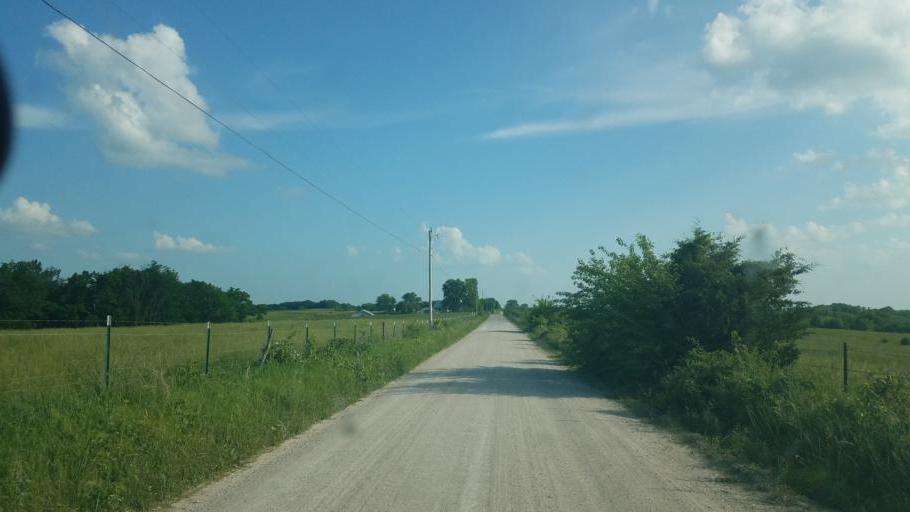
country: US
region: Missouri
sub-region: Moniteau County
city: California
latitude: 38.7560
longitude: -92.6055
